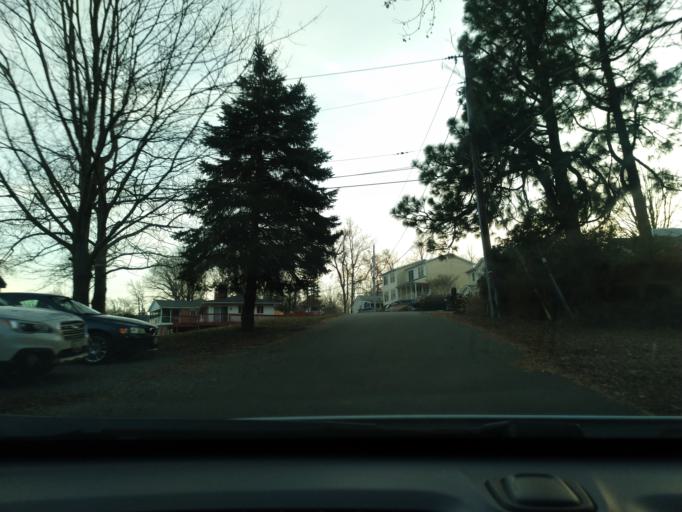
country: US
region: Maryland
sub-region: Calvert County
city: Chesapeake Beach
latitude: 38.6300
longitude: -76.5184
